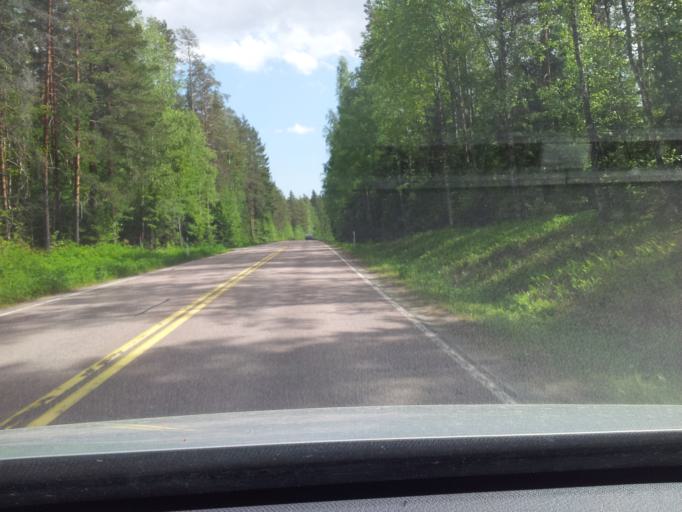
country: FI
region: South Karelia
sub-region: Lappeenranta
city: Luumaeki
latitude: 60.9649
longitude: 27.5686
